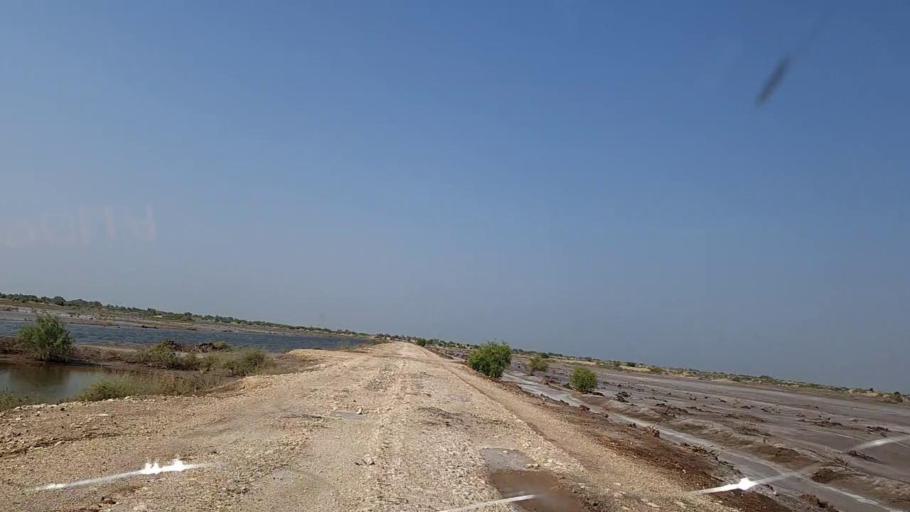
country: PK
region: Sindh
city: Khanpur
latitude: 27.6913
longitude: 69.3826
